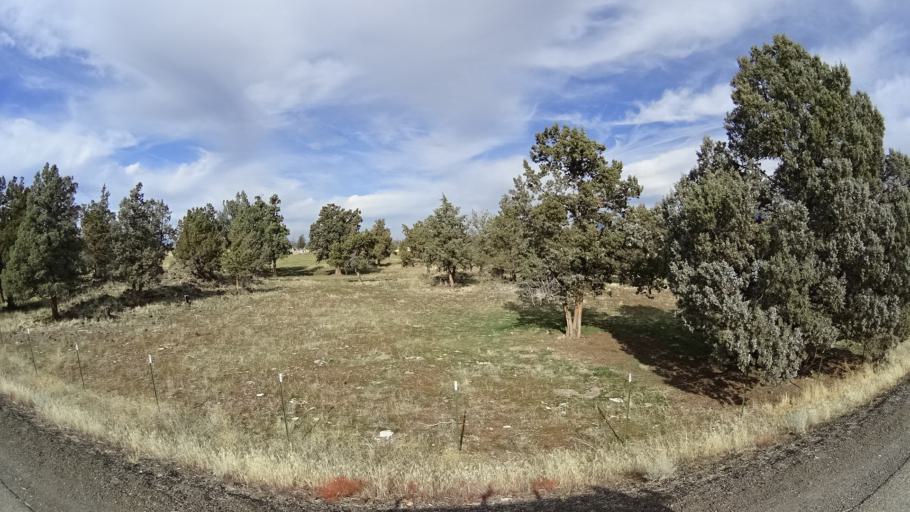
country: US
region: California
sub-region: Siskiyou County
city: Montague
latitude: 41.6093
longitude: -122.4002
